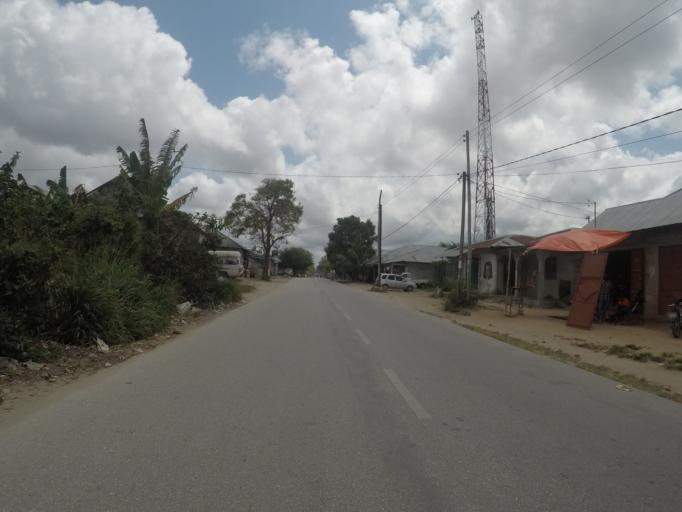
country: TZ
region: Zanzibar Urban/West
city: Zanzibar
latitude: -6.1969
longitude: 39.2440
